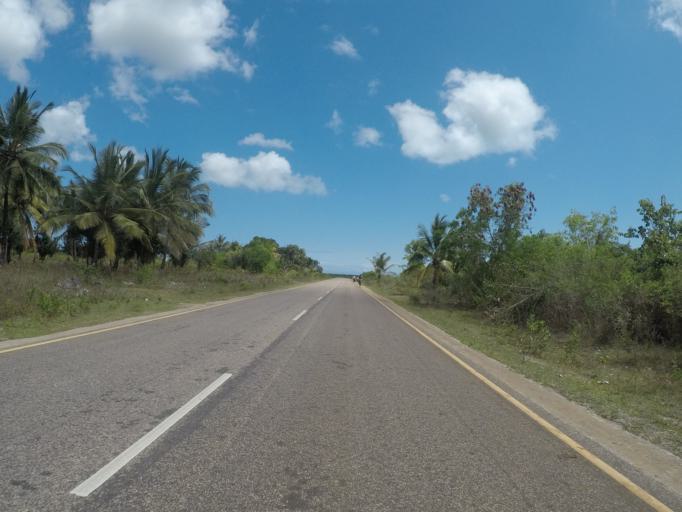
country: TZ
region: Zanzibar Central/South
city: Koani
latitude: -6.2457
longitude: 39.3556
